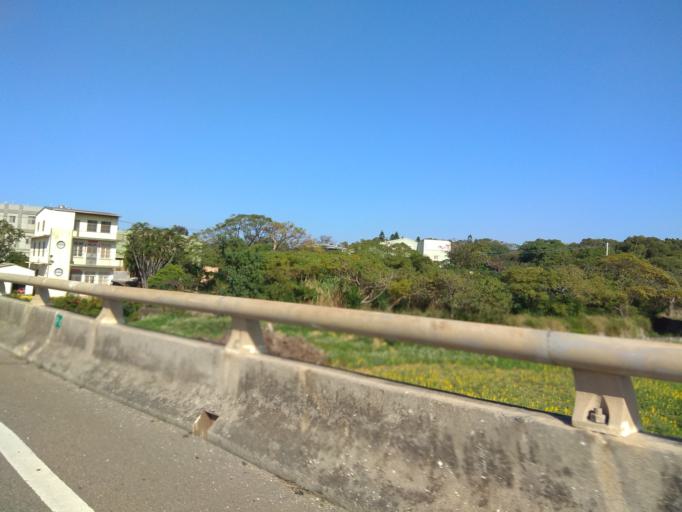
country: TW
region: Taiwan
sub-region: Hsinchu
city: Zhubei
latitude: 24.9970
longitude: 121.0350
